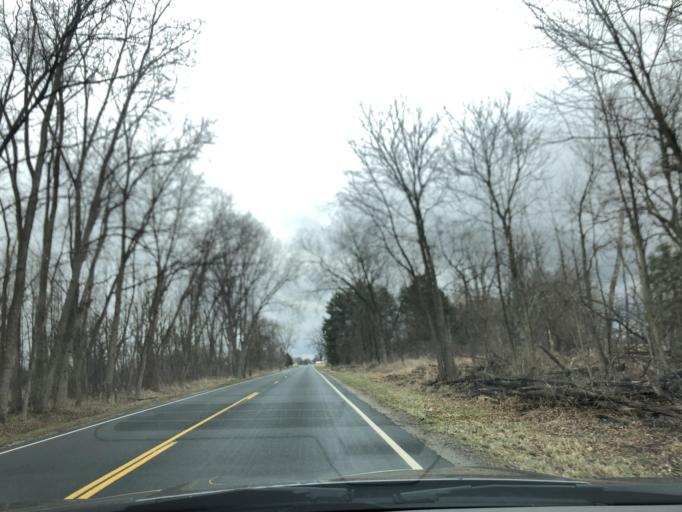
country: US
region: Michigan
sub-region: Clinton County
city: Saint Johns
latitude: 43.0462
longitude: -84.6301
